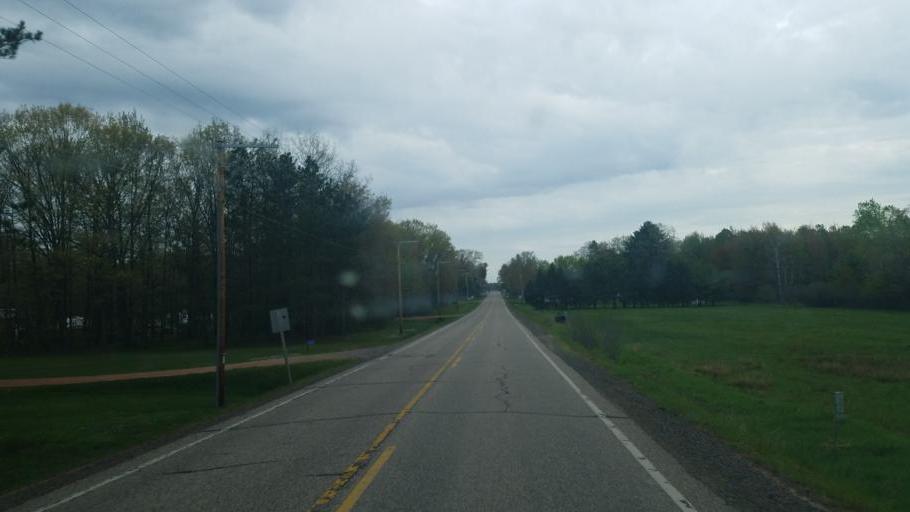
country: US
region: Wisconsin
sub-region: Wood County
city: Marshfield
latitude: 44.5495
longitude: -90.3000
